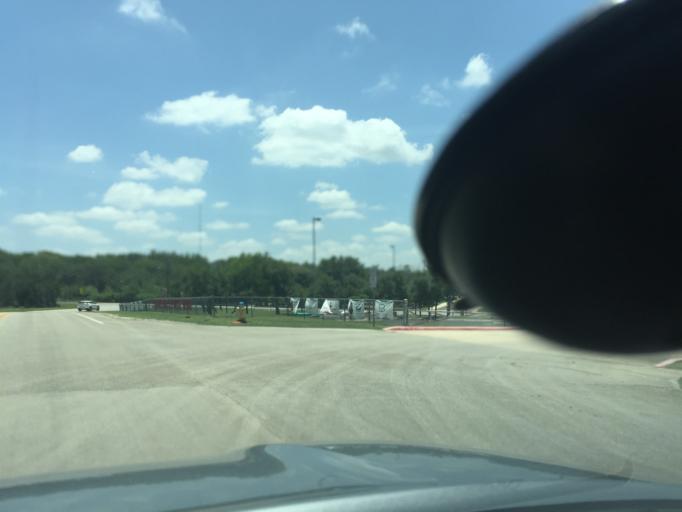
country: US
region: Texas
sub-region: Bexar County
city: Timberwood Park
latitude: 29.7074
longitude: -98.5097
